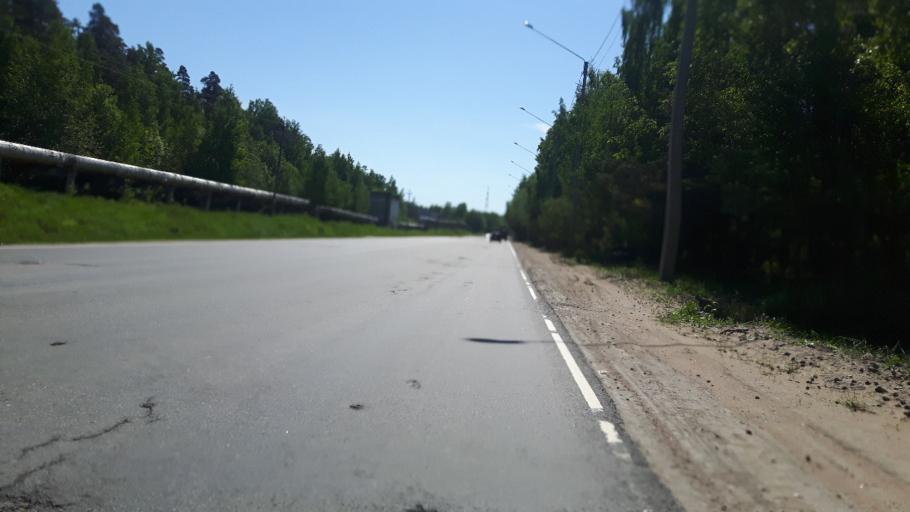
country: RU
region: Leningrad
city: Sosnovyy Bor
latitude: 59.8628
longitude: 29.0665
